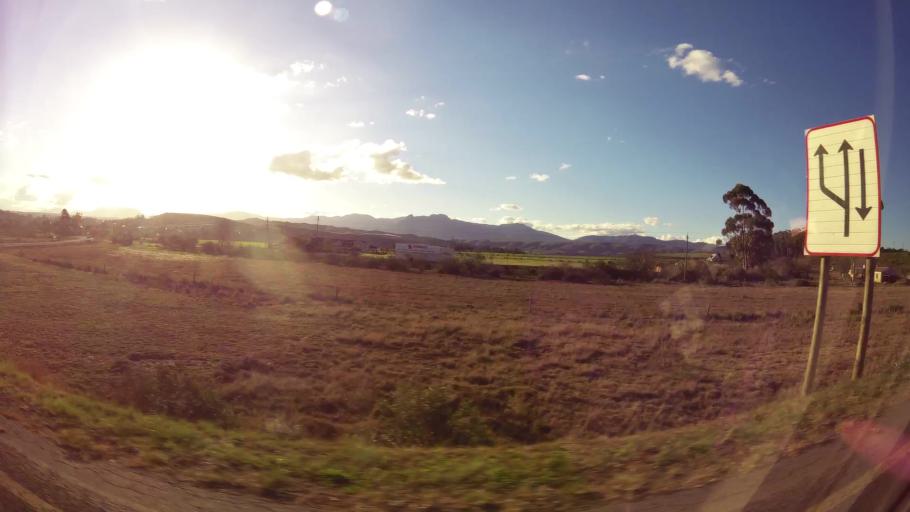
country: ZA
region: Western Cape
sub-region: Eden District Municipality
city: Riversdale
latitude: -34.0930
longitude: 20.9734
